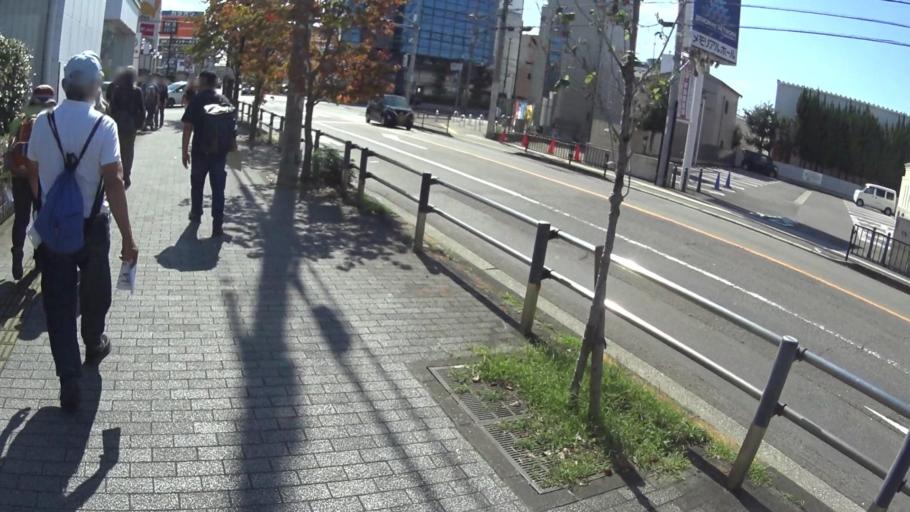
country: JP
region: Ehime
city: Kihoku-cho
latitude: 33.3909
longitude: 132.8450
